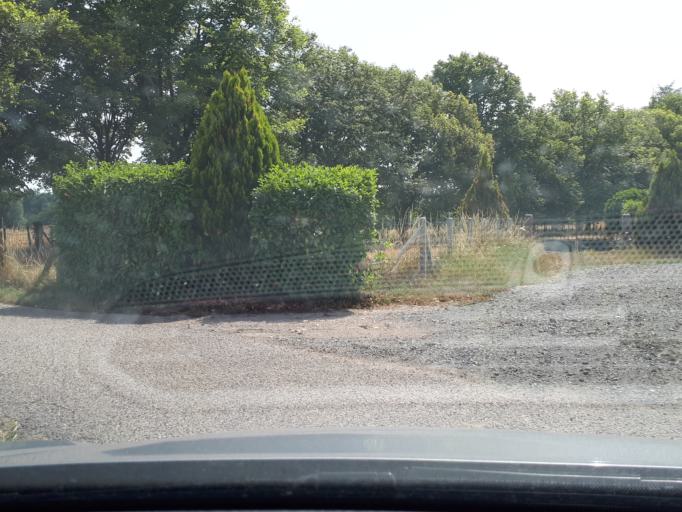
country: FR
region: Rhone-Alpes
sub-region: Departement de la Loire
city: Civens
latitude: 45.7510
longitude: 4.2671
